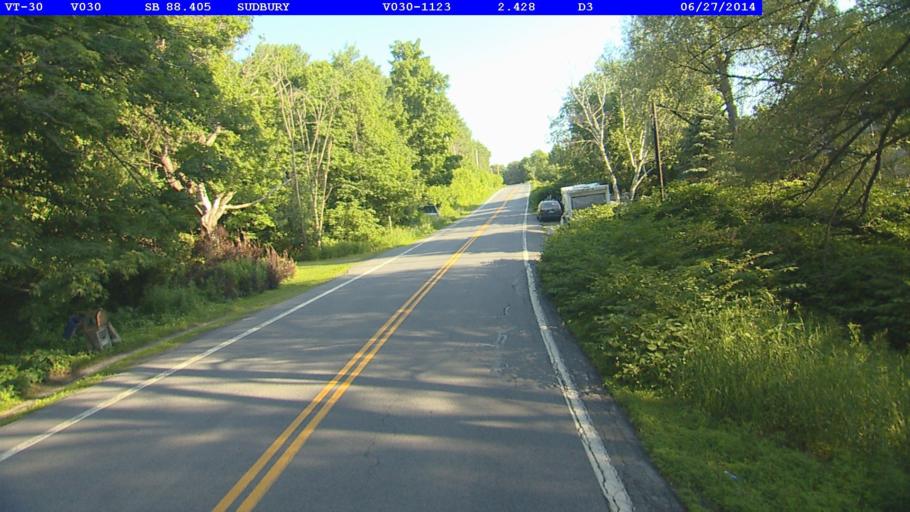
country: US
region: Vermont
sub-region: Rutland County
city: Brandon
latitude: 43.7830
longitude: -73.2029
